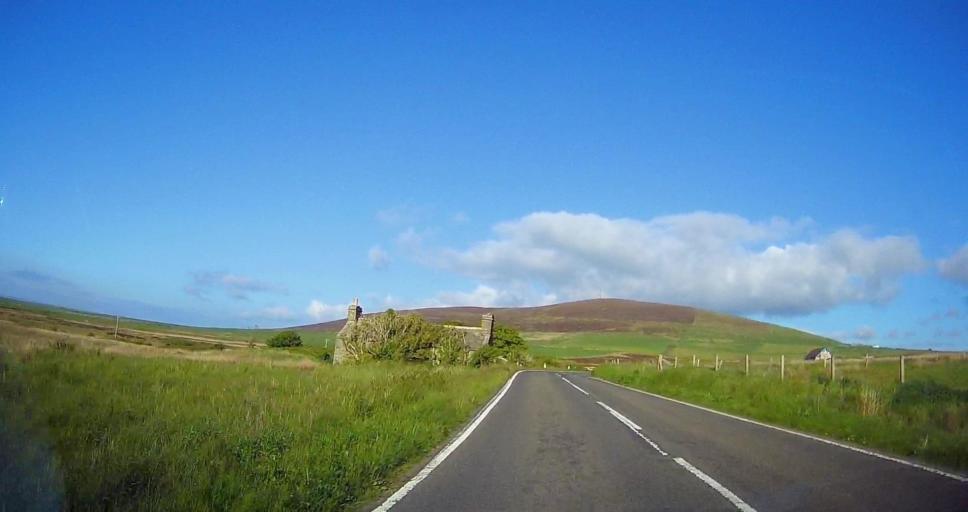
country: GB
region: Scotland
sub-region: Orkney Islands
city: Orkney
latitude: 58.9883
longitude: -3.0586
